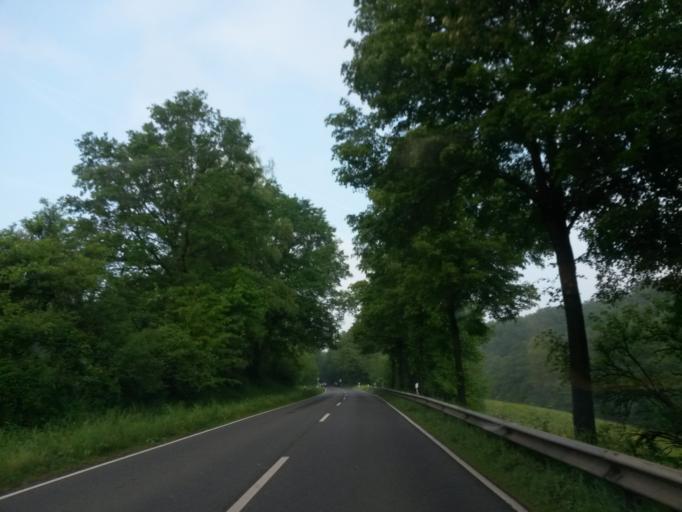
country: DE
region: North Rhine-Westphalia
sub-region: Regierungsbezirk Koln
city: Hennef
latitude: 50.8447
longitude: 7.3151
